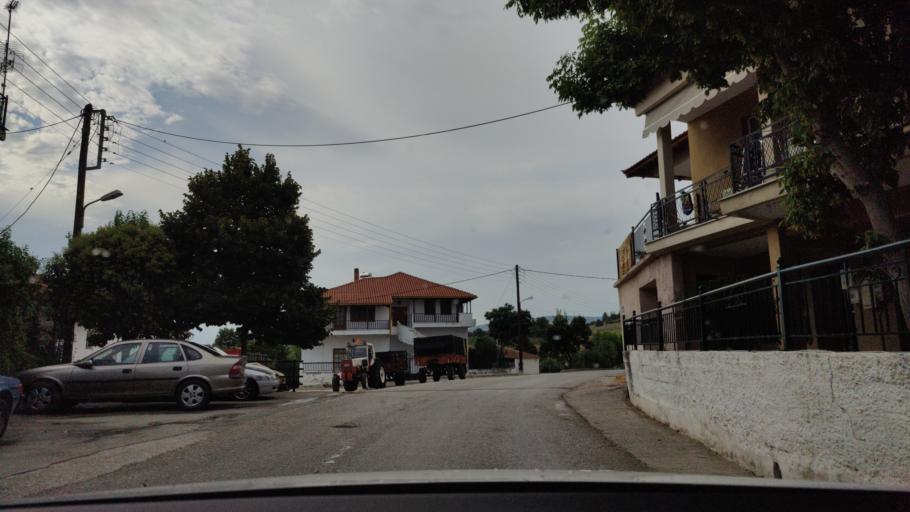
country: GR
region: Central Macedonia
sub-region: Nomos Serron
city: Lefkonas
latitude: 41.1200
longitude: 23.4602
